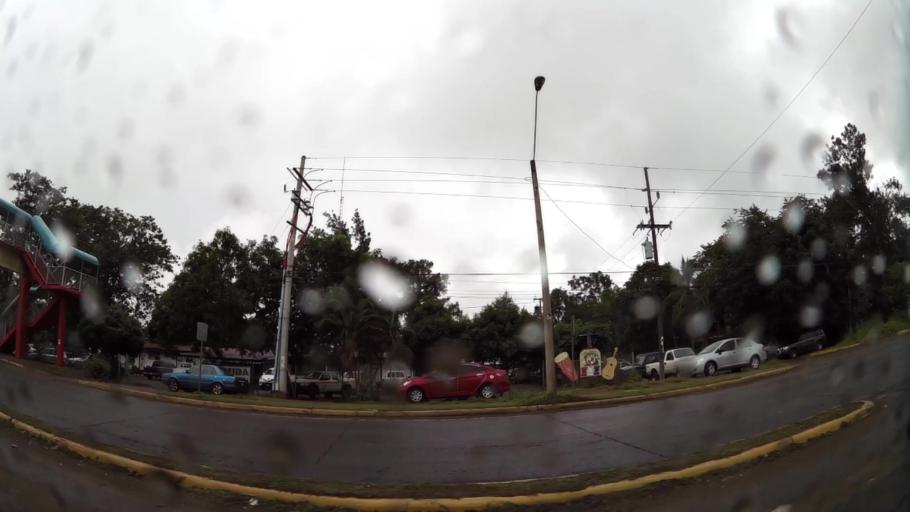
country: PA
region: Chiriqui
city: David
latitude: 8.4395
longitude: -82.4362
